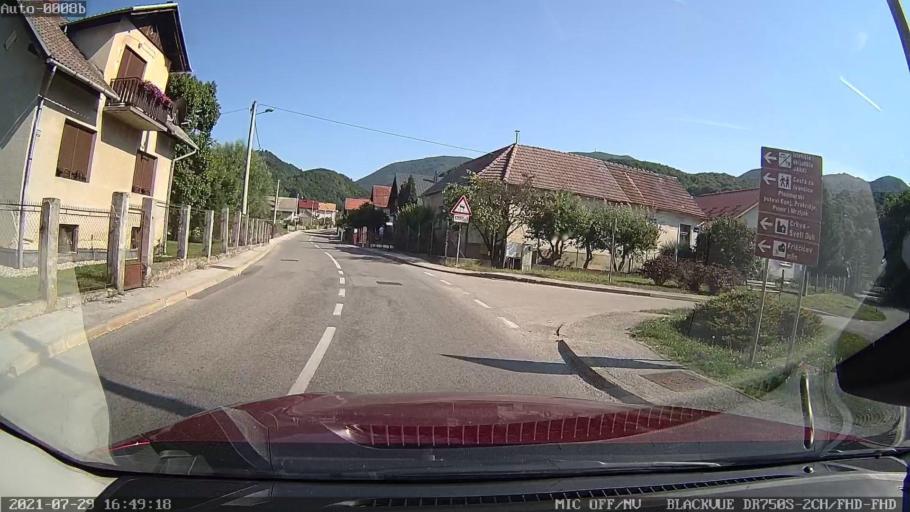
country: HR
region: Varazdinska
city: Ivanec
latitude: 46.2157
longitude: 16.1265
